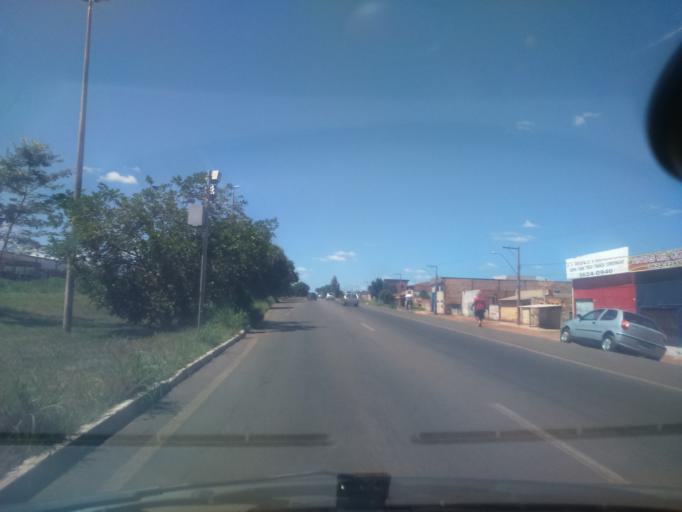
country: BR
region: Goias
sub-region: Luziania
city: Luziania
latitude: -16.0492
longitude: -47.9983
